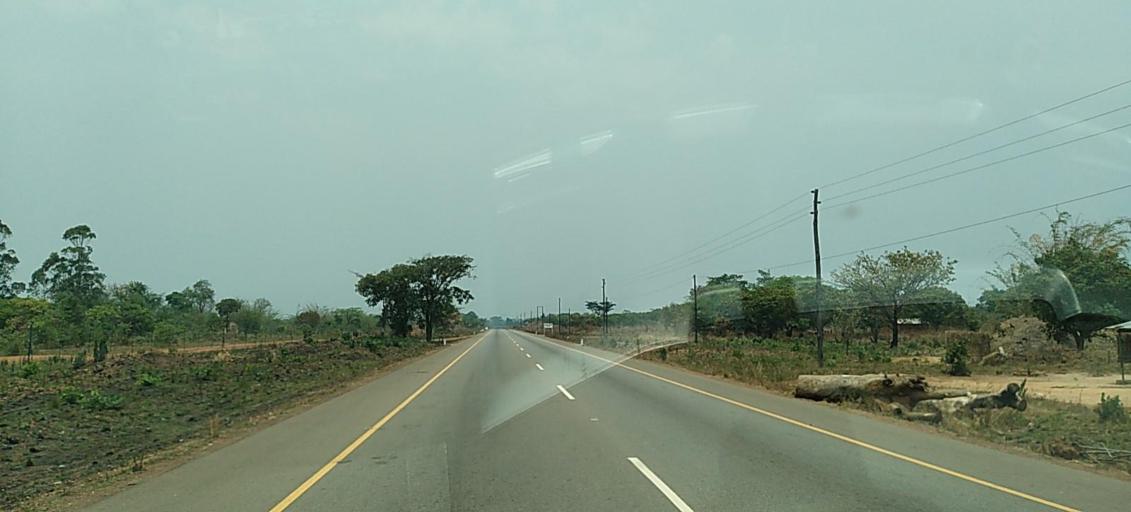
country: ZM
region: Copperbelt
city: Chililabombwe
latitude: -12.5369
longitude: 27.6038
